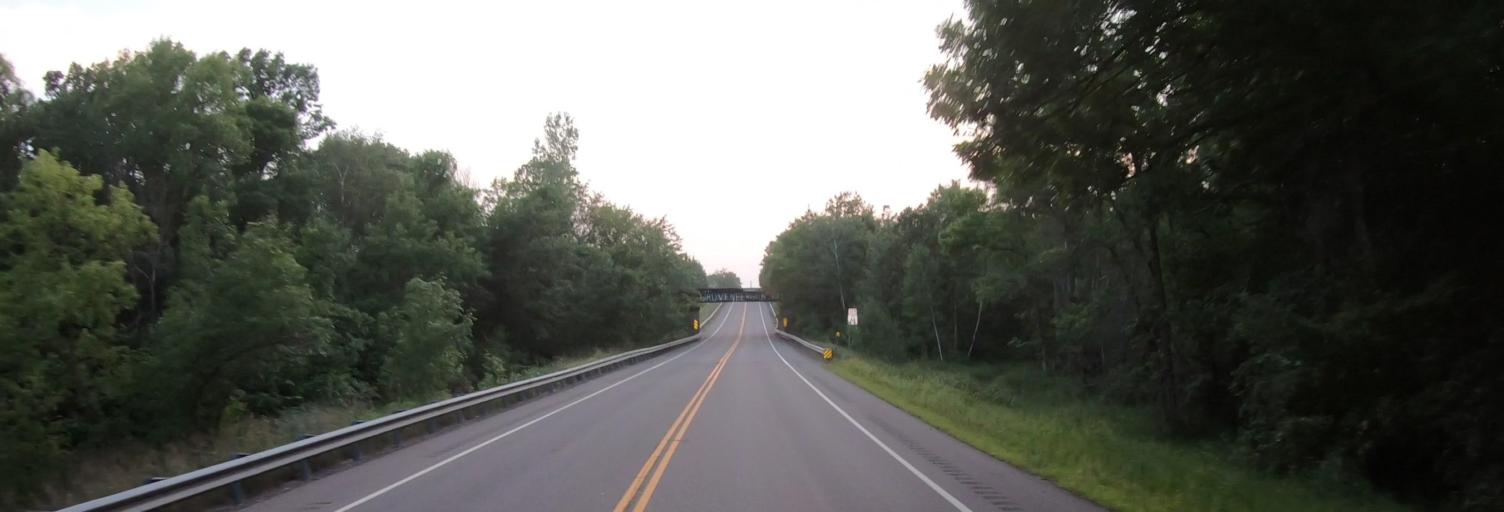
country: US
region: Minnesota
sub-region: Pine County
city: Rock Creek
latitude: 45.7664
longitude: -92.9619
